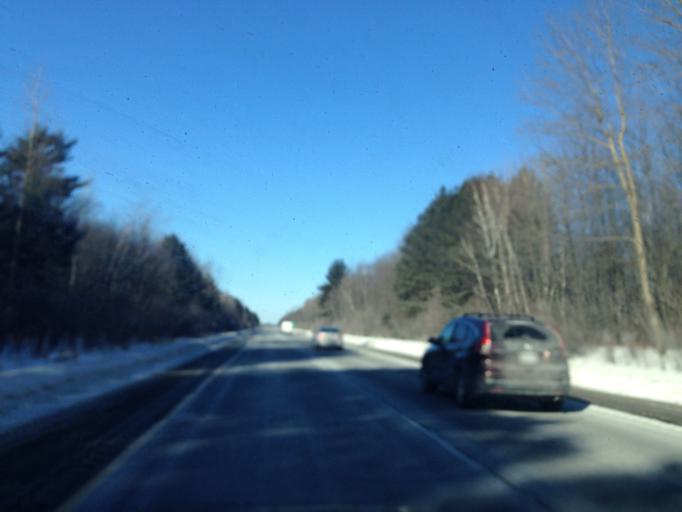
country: CA
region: Ontario
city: Ottawa
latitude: 45.3637
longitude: -75.4948
